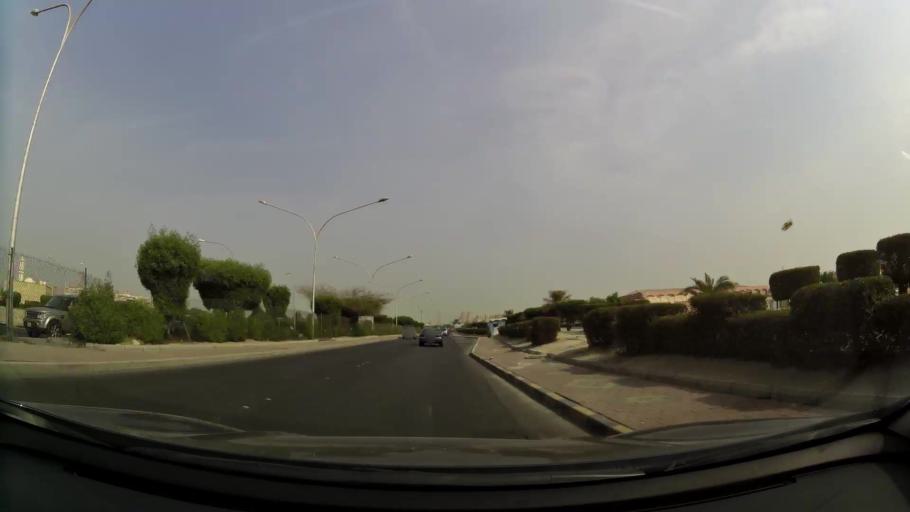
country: KW
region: Al Asimah
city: Ar Rabiyah
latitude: 29.2888
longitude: 47.9392
